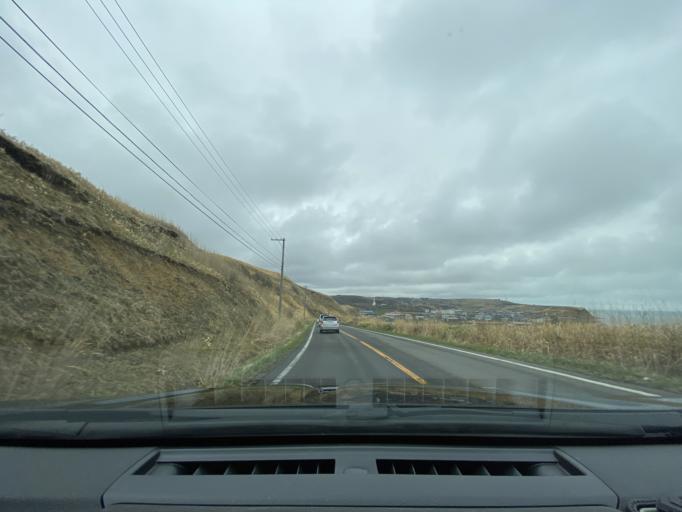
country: JP
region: Hokkaido
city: Ishikari
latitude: 43.3205
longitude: 141.4208
